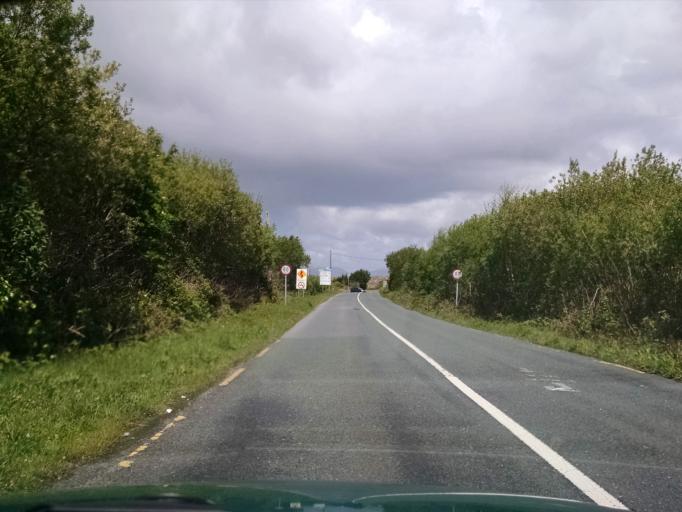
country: IE
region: Connaught
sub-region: County Galway
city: Oughterard
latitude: 53.2911
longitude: -9.5493
